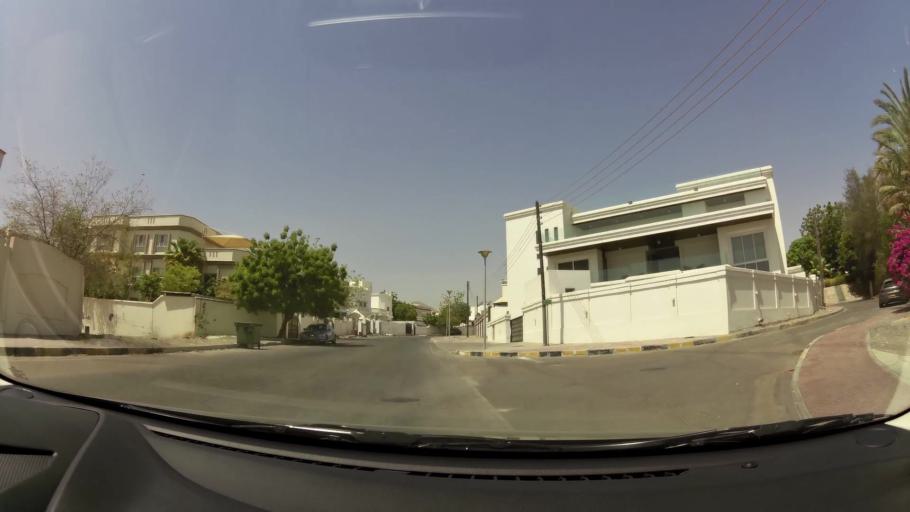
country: OM
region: Muhafazat Masqat
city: Bawshar
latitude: 23.5923
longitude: 58.4559
